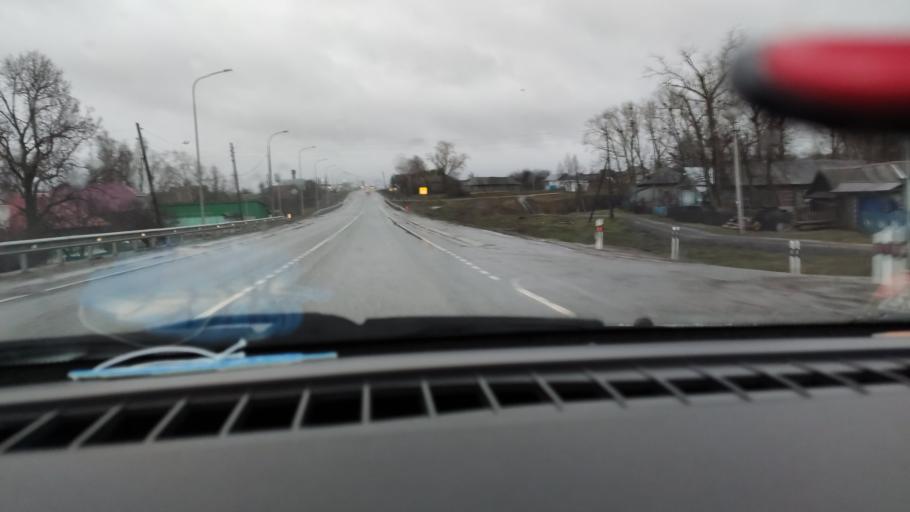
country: RU
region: Tatarstan
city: Mendeleyevsk
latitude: 56.0298
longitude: 52.3743
